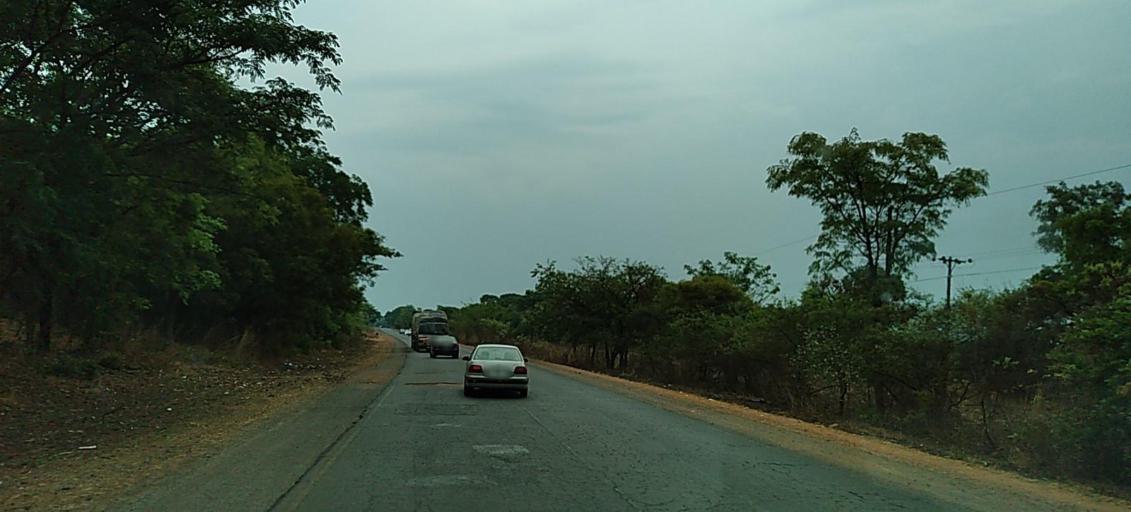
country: ZM
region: Copperbelt
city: Luanshya
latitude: -13.0861
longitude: 28.4382
